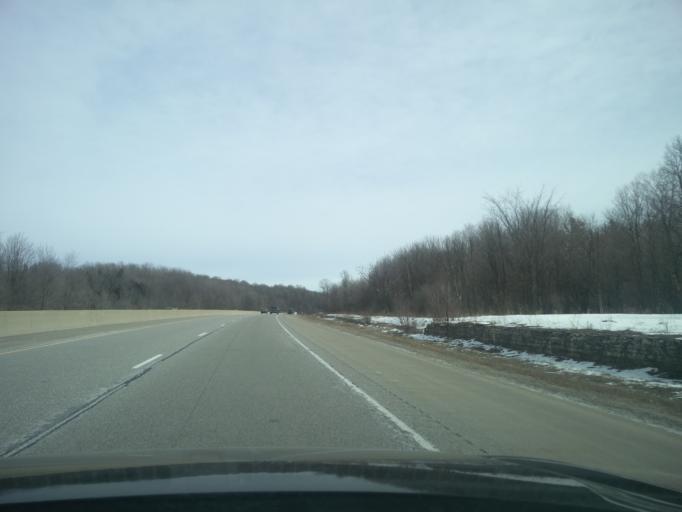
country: CA
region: Ontario
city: Brockville
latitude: 44.5461
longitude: -75.7674
